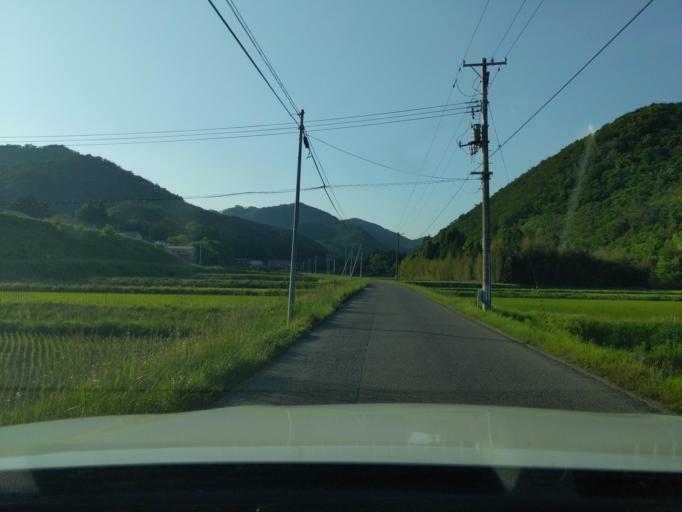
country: JP
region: Fukushima
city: Motomiya
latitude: 37.4942
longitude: 140.3280
